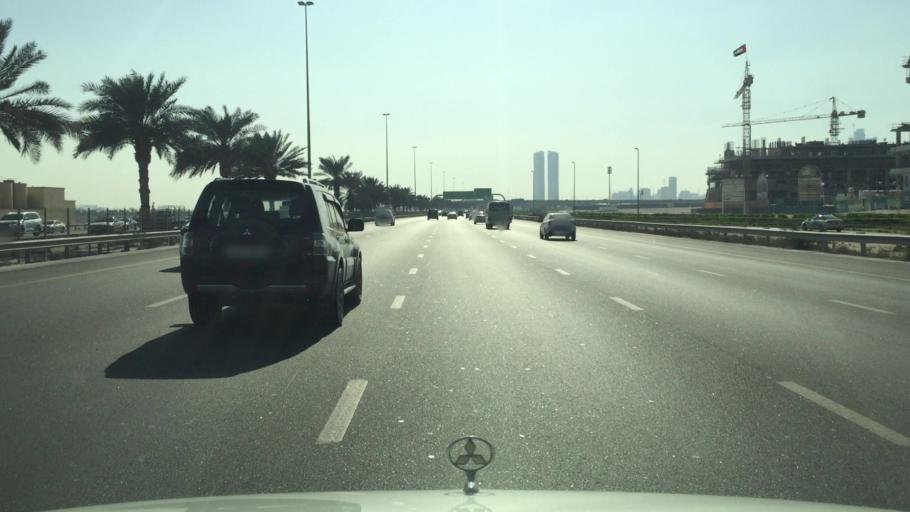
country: AE
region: Ash Shariqah
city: Sharjah
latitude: 25.2135
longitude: 55.3219
